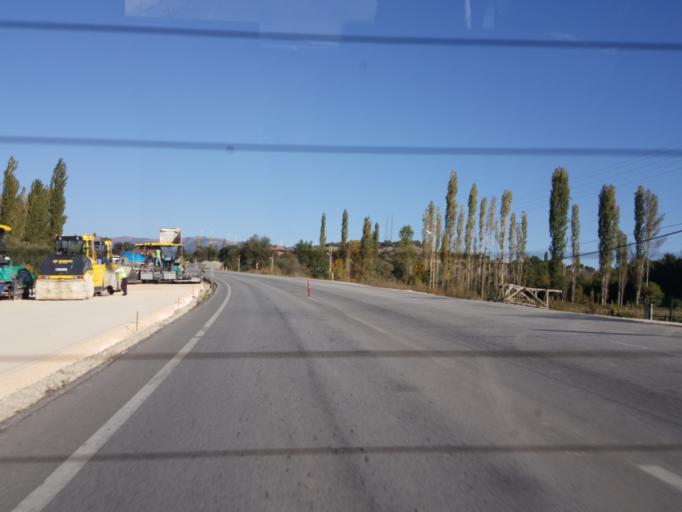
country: TR
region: Amasya
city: Ezinepazari
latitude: 40.5479
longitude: 36.1511
